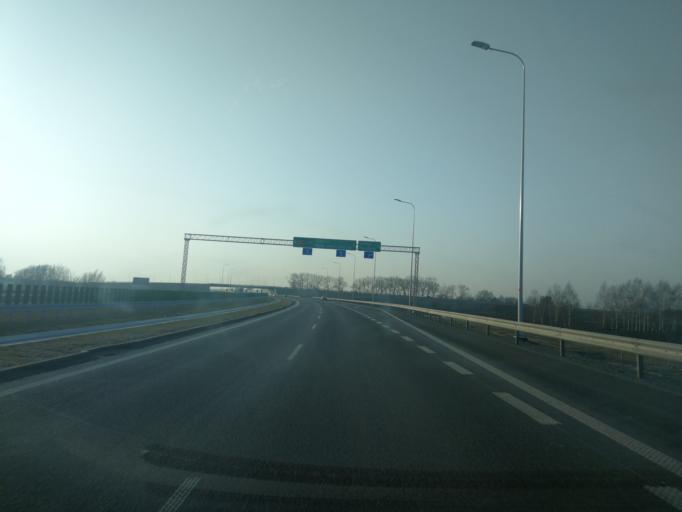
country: PL
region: Warmian-Masurian Voivodeship
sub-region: Powiat elblaski
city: Elblag
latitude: 54.1630
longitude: 19.3526
